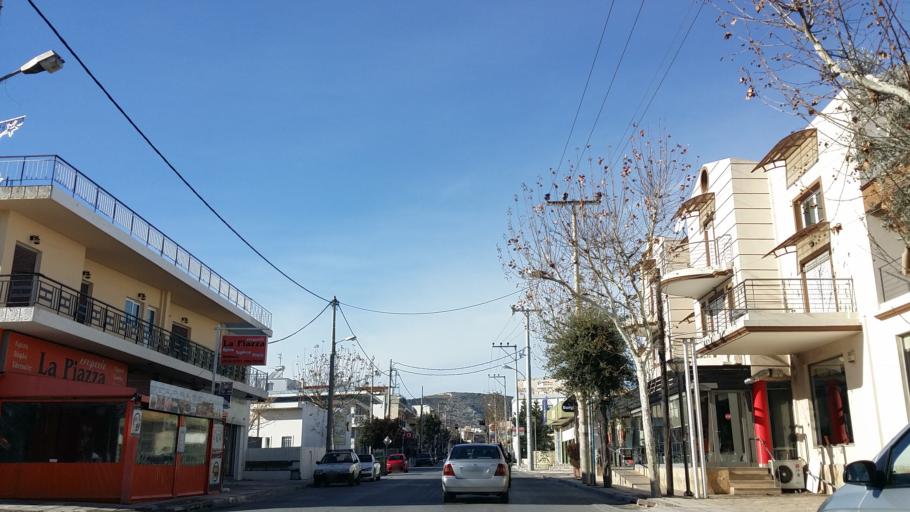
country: GR
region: Attica
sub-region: Nomarchia Dytikis Attikis
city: Ano Liosia
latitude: 38.0765
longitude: 23.7036
